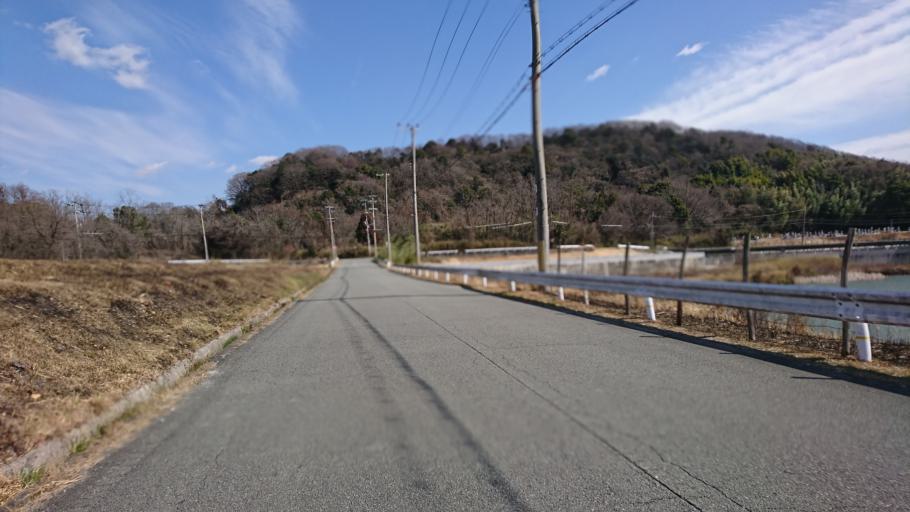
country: JP
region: Hyogo
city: Kakogawacho-honmachi
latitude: 34.8299
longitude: 134.8202
